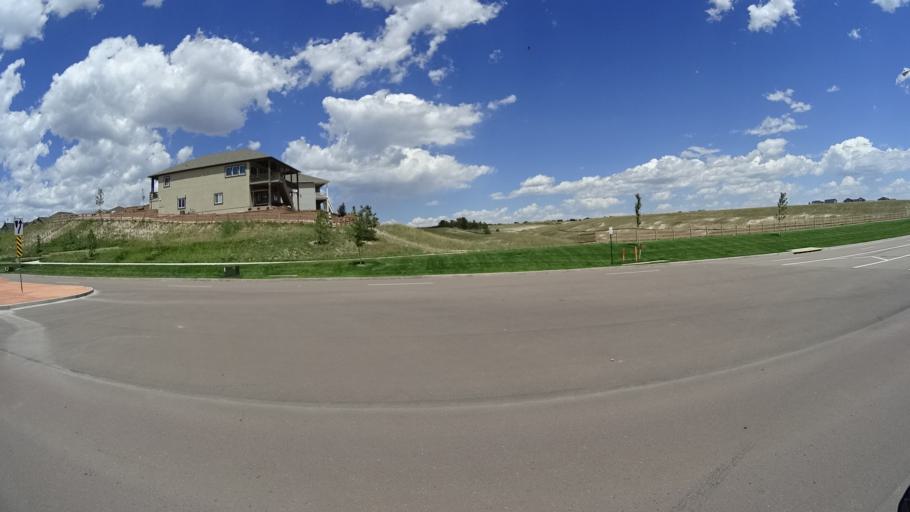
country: US
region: Colorado
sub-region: El Paso County
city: Black Forest
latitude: 38.9609
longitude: -104.7118
